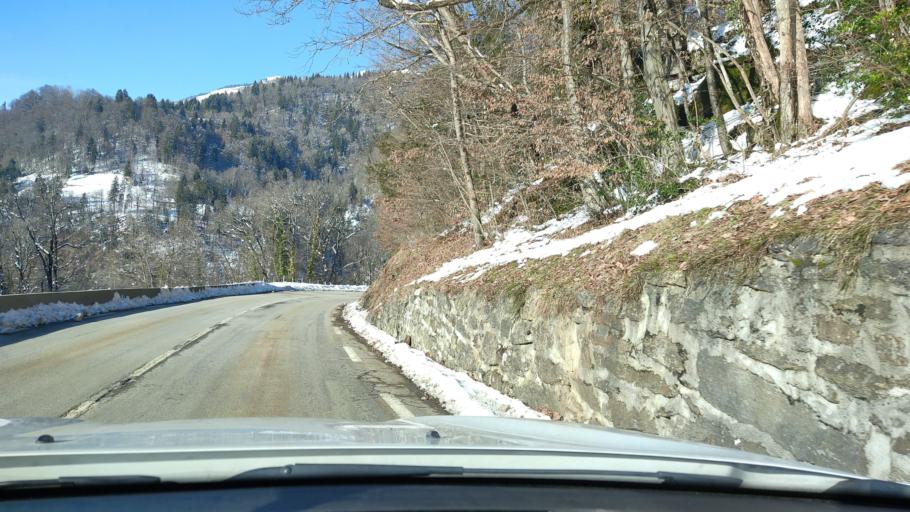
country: FR
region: Rhone-Alpes
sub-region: Departement de la Savoie
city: Ugine
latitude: 45.7553
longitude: 6.4453
